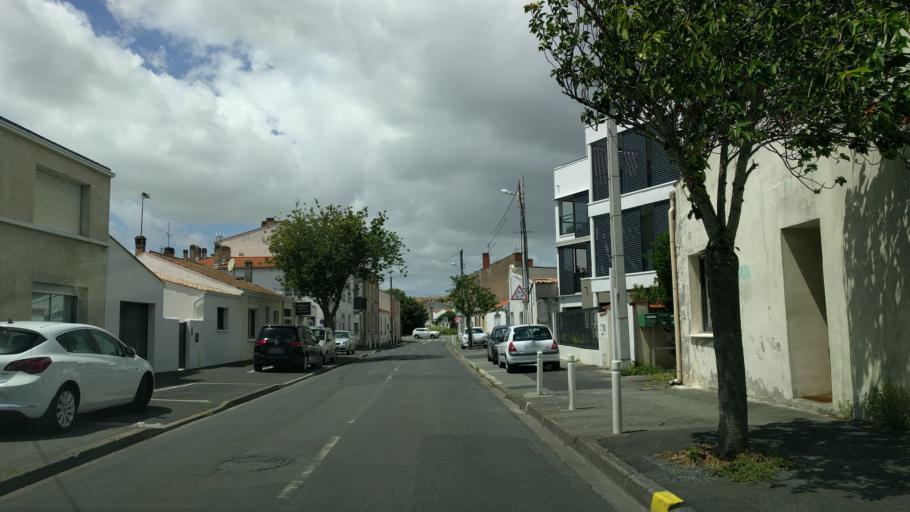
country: FR
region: Poitou-Charentes
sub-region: Departement de la Charente-Maritime
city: La Rochelle
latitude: 46.1630
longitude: -1.1371
